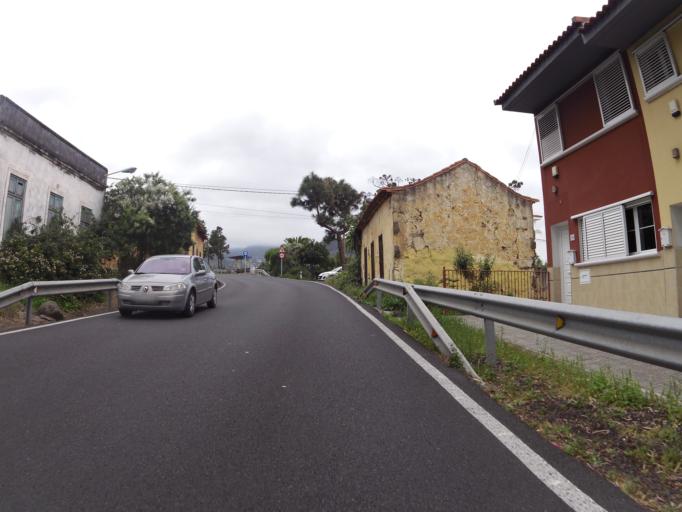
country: ES
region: Canary Islands
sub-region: Provincia de Las Palmas
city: Arucas
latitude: 28.0928
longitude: -15.5042
